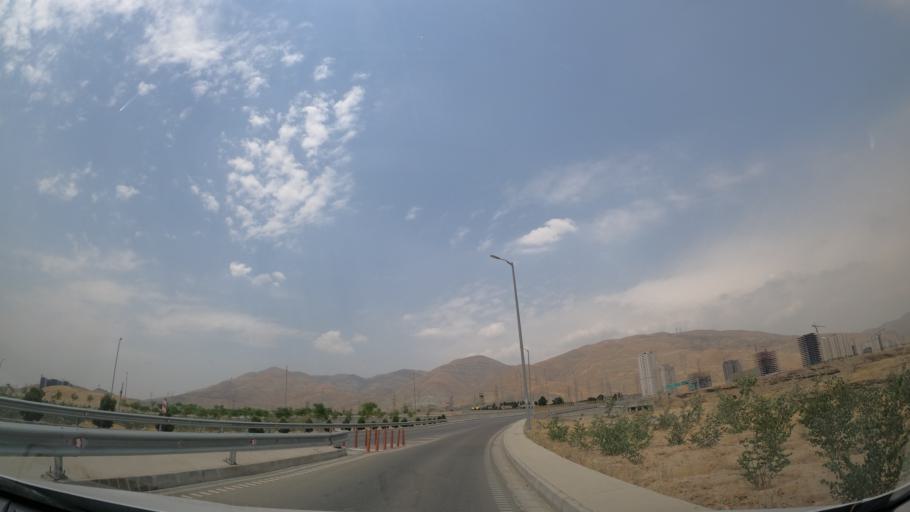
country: IR
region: Tehran
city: Shahr-e Qods
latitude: 35.7448
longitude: 51.1281
